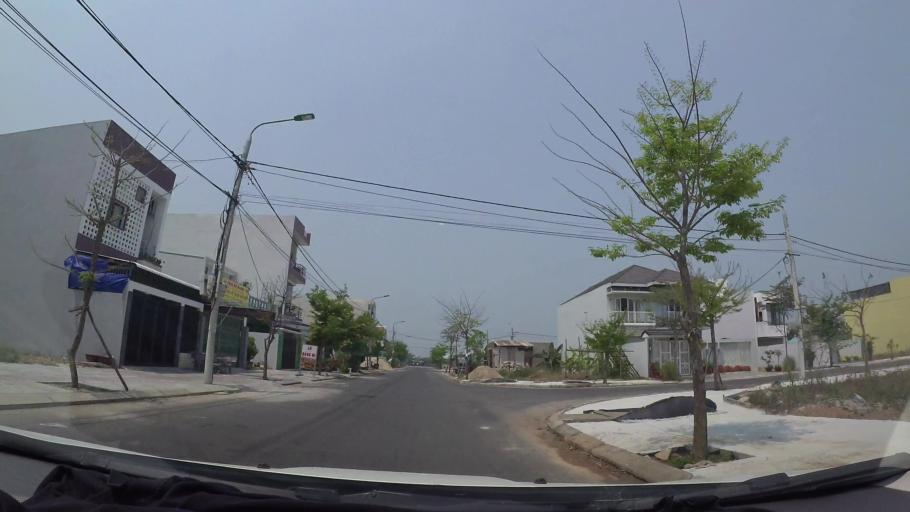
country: VN
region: Da Nang
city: Cam Le
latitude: 16.0172
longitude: 108.2209
